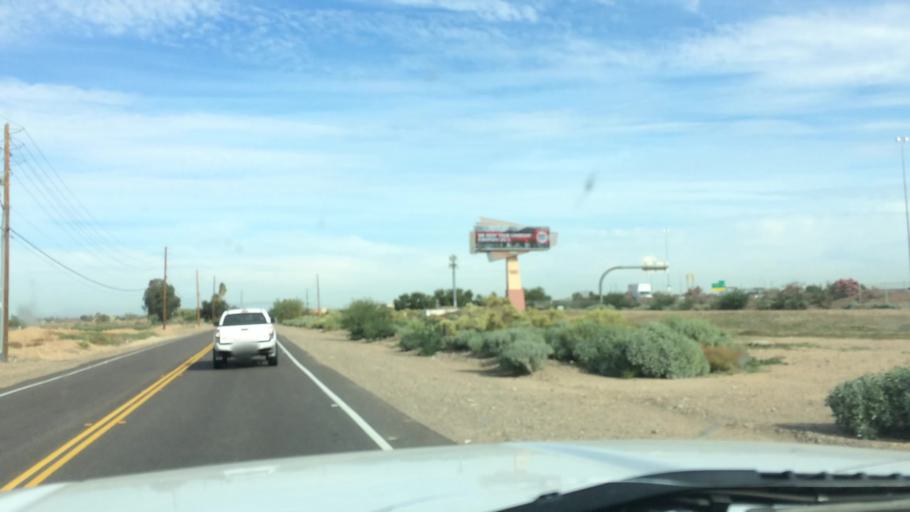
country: US
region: Arizona
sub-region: Maricopa County
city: Peoria
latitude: 33.5444
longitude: -112.2725
